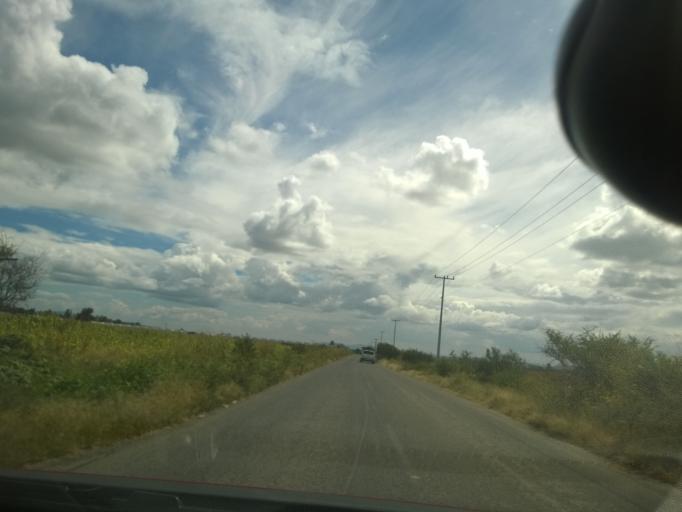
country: MX
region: Guanajuato
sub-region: Leon
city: El CERESO
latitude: 20.9745
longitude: -101.6531
